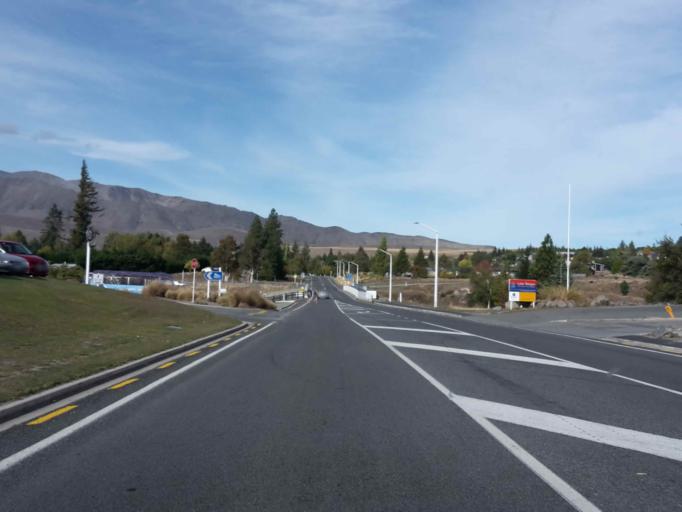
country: NZ
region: Canterbury
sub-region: Timaru District
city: Pleasant Point
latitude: -44.0058
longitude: 170.4787
